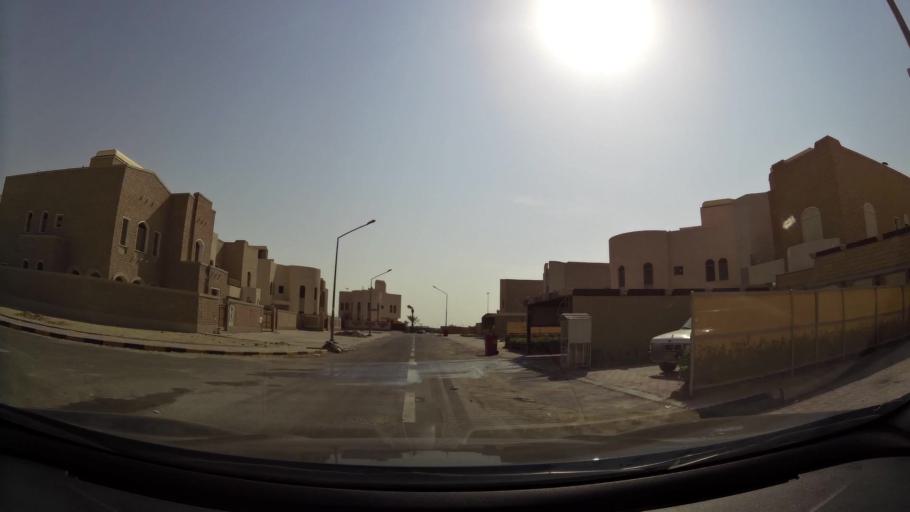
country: KW
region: Al Ahmadi
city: Al Wafrah
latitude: 28.7966
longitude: 48.0771
